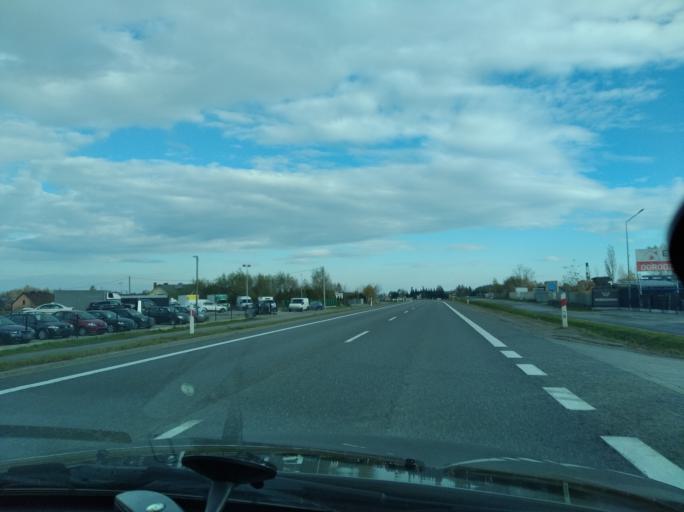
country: PL
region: Subcarpathian Voivodeship
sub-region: Powiat debicki
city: Debica
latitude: 50.0497
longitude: 21.4461
